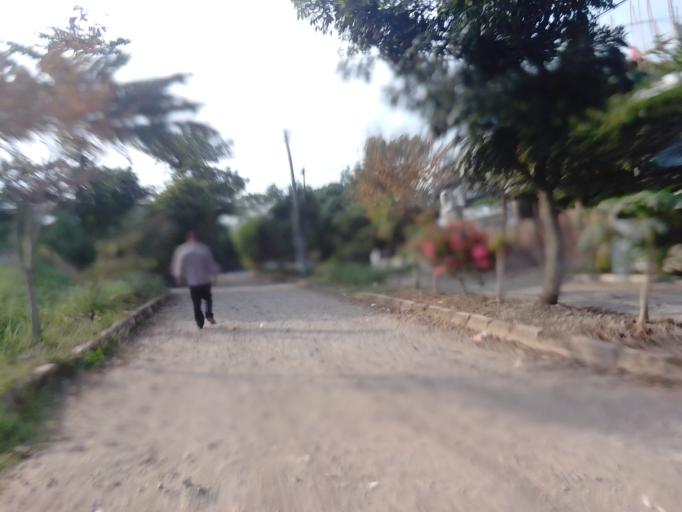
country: ID
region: West Java
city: Cileunyi
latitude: -6.9327
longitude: 107.7133
